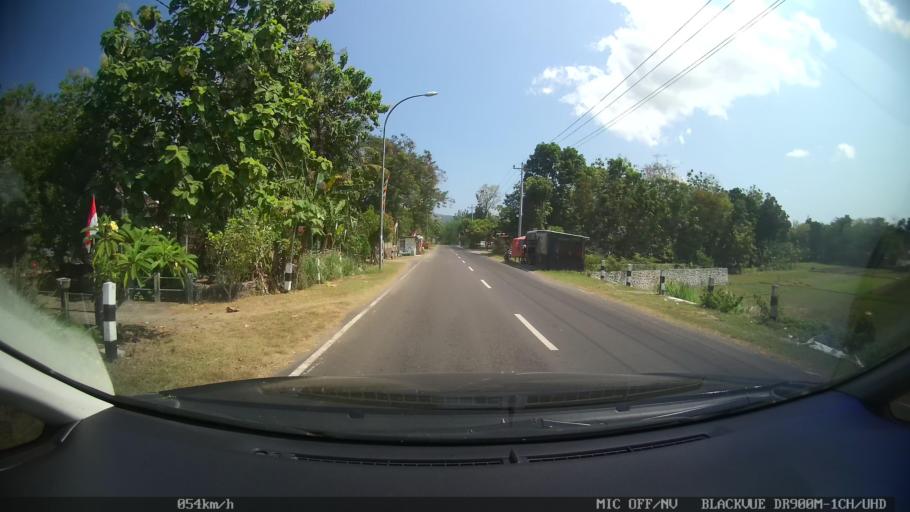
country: ID
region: Daerah Istimewa Yogyakarta
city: Pundong
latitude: -7.9614
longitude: 110.3568
